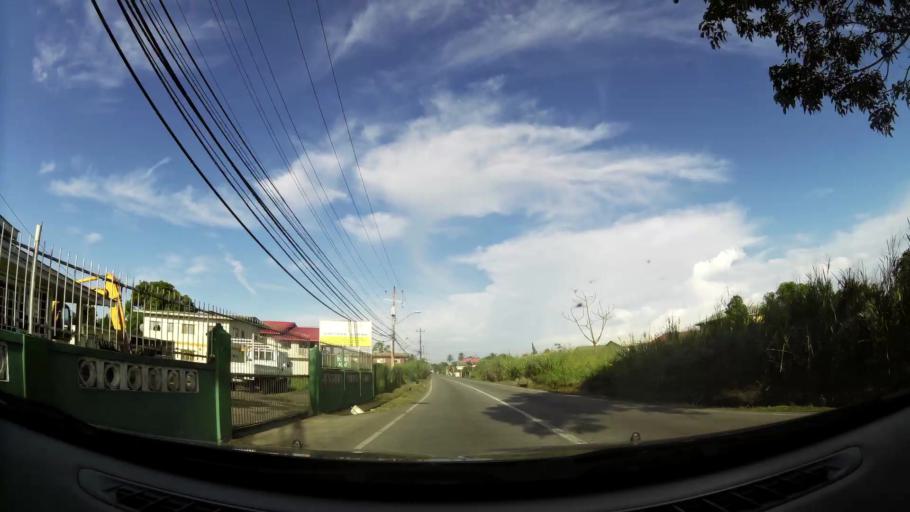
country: TT
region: Chaguanas
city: Chaguanas
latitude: 10.5481
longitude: -61.3548
